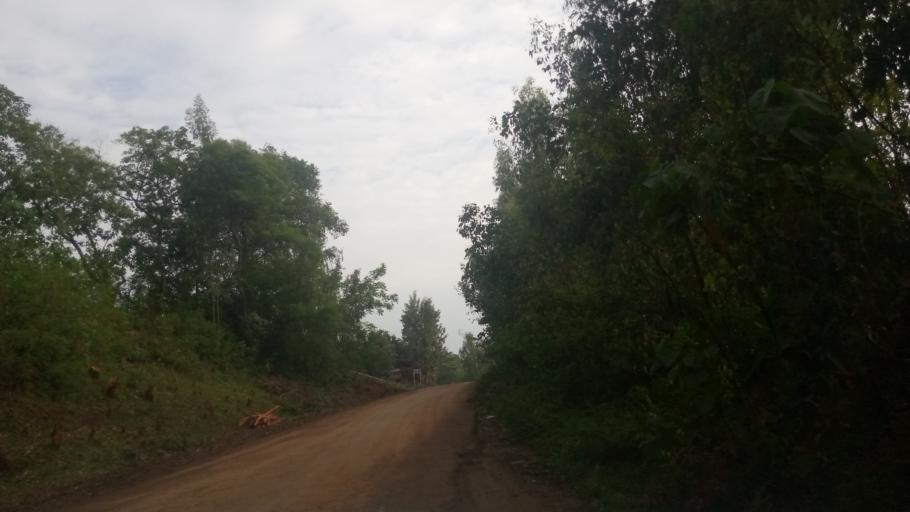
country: ET
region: Oromiya
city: Agaro
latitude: 7.8465
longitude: 36.6574
